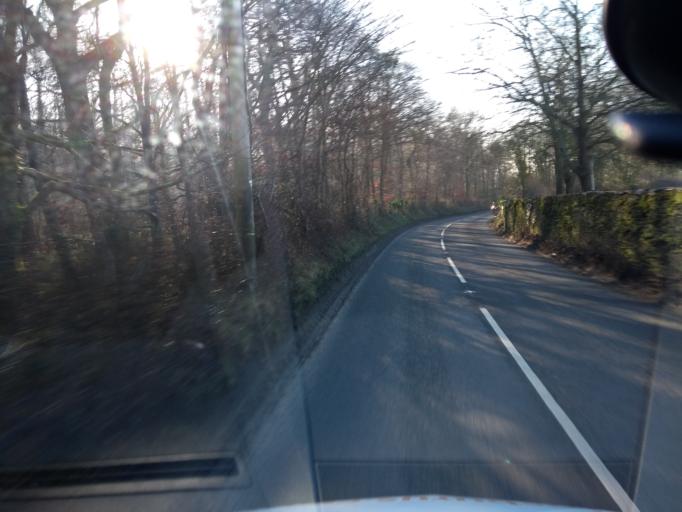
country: GB
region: England
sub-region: Somerset
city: Redlynch
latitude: 51.0947
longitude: -2.4194
